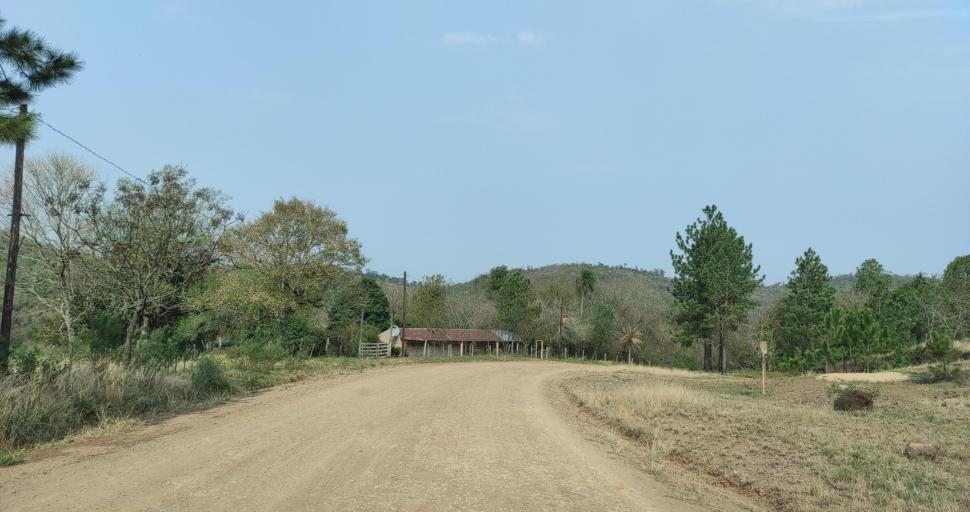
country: AR
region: Misiones
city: Cerro Cora
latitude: -27.5542
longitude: -55.5790
